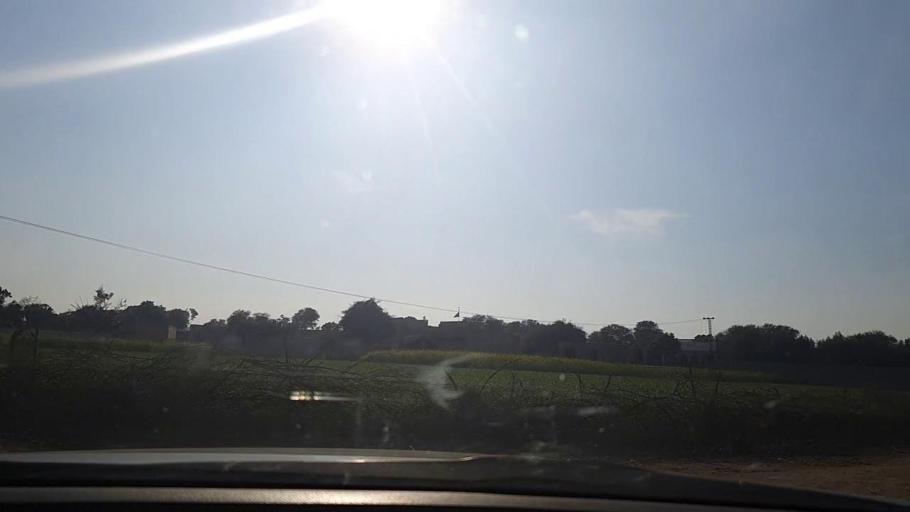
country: PK
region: Sindh
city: Sehwan
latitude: 26.2998
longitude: 67.9877
